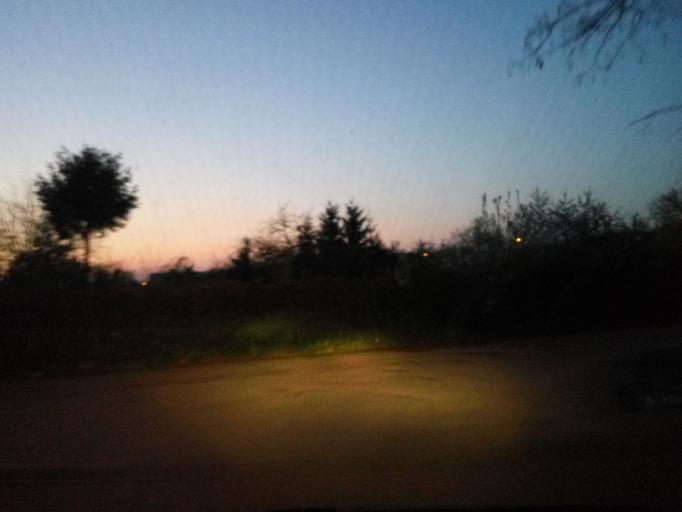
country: PL
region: Lower Silesian Voivodeship
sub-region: Powiat wroclawski
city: Radwanice
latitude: 51.0759
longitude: 17.0817
